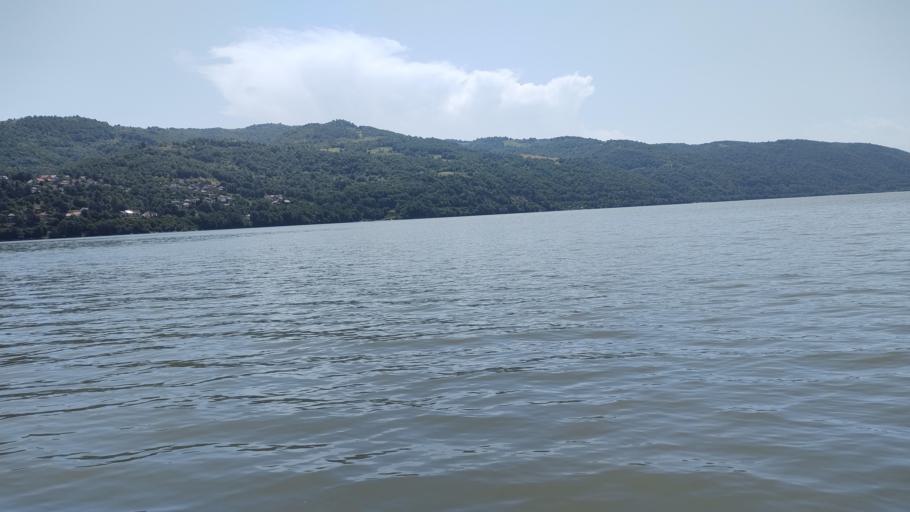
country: RO
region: Mehedinti
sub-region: Comuna Svinita
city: Svinita
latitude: 44.5023
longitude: 22.1911
